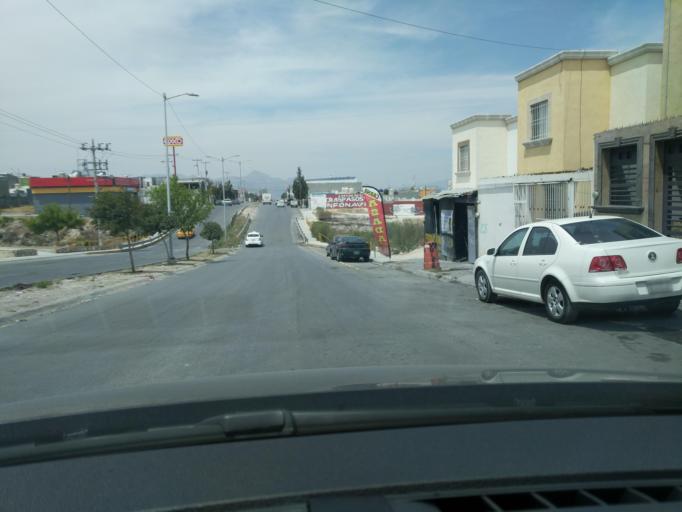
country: MX
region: Coahuila
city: Saltillo
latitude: 25.3532
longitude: -101.0143
